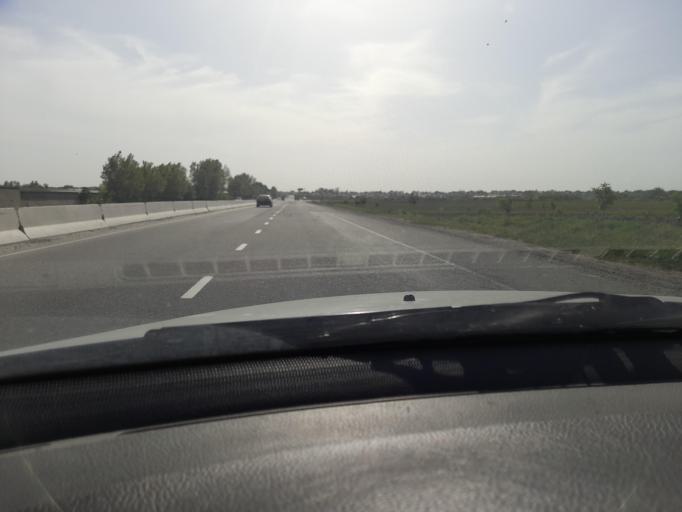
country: UZ
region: Samarqand
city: Kattaqo'rg'on
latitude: 39.9192
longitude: 66.3375
